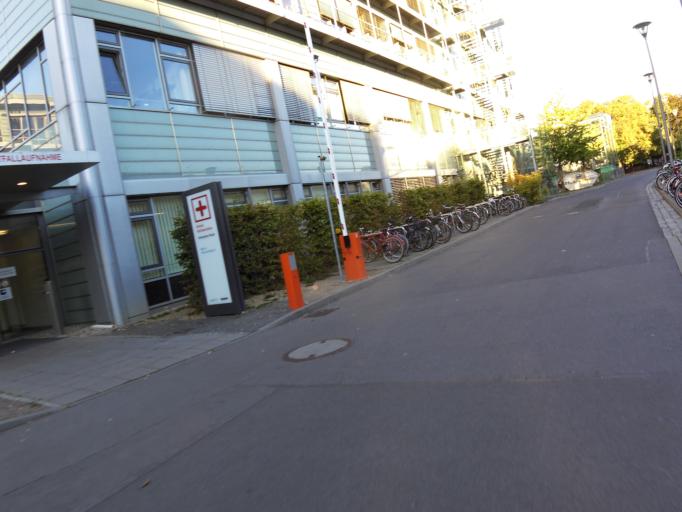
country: DE
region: Saxony
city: Leipzig
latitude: 51.3300
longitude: 12.3865
